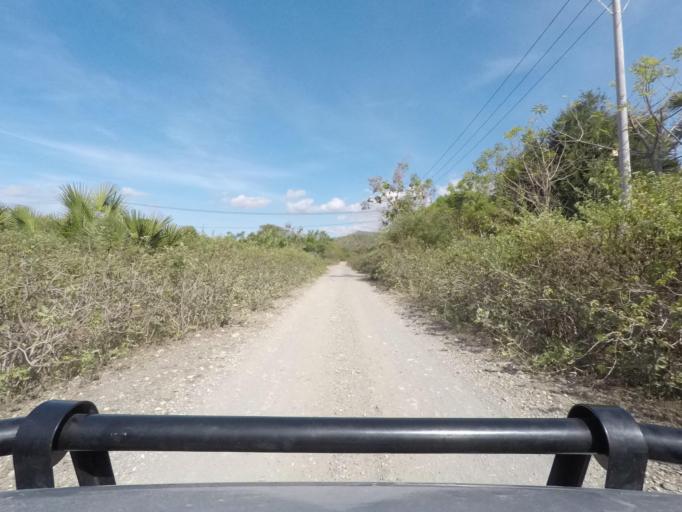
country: ID
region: East Nusa Tenggara
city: Atambua
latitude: -8.9578
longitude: 124.9604
